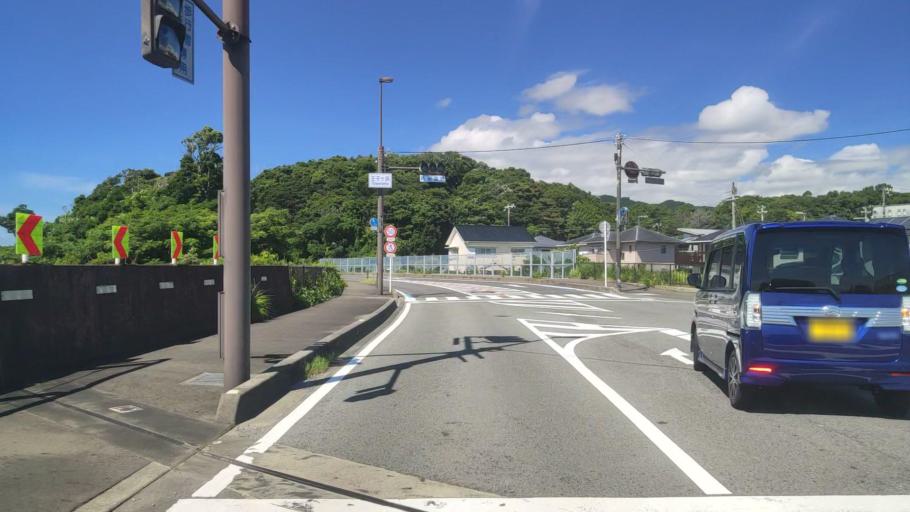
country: JP
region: Wakayama
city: Shingu
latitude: 33.7143
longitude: 136.0008
